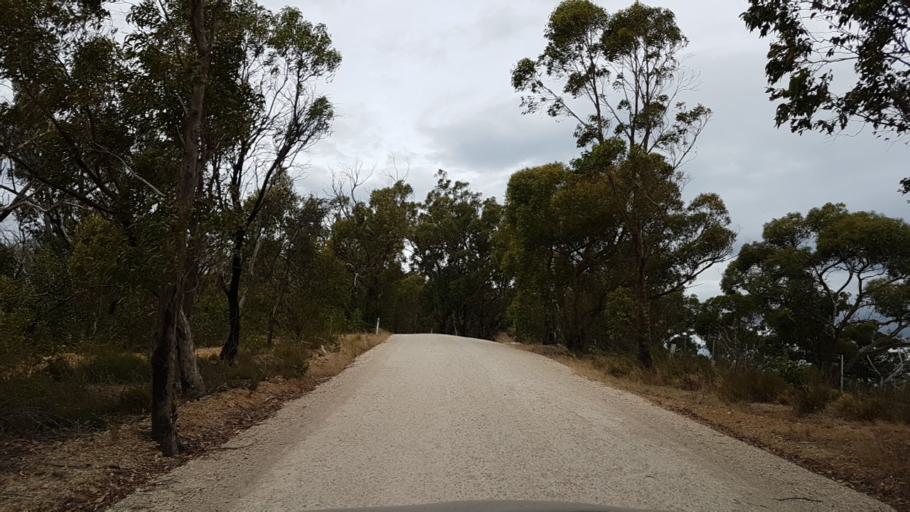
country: AU
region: South Australia
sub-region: Tea Tree Gully
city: Golden Grove
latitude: -34.7787
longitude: 138.8129
